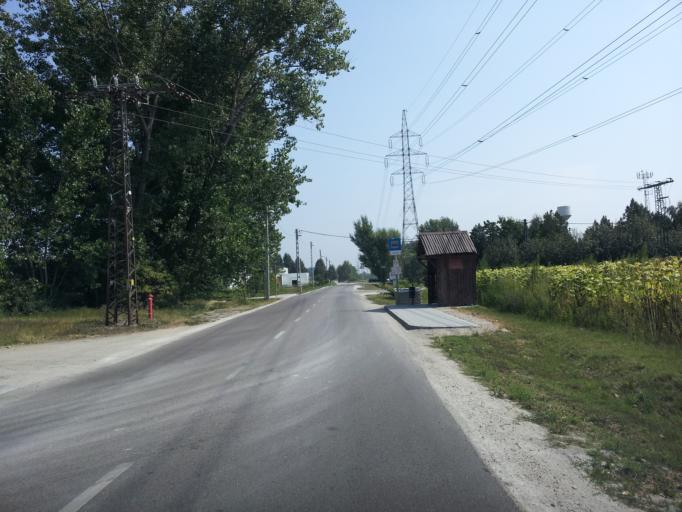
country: HU
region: Pest
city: Dunavarsany
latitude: 47.2853
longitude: 19.0497
